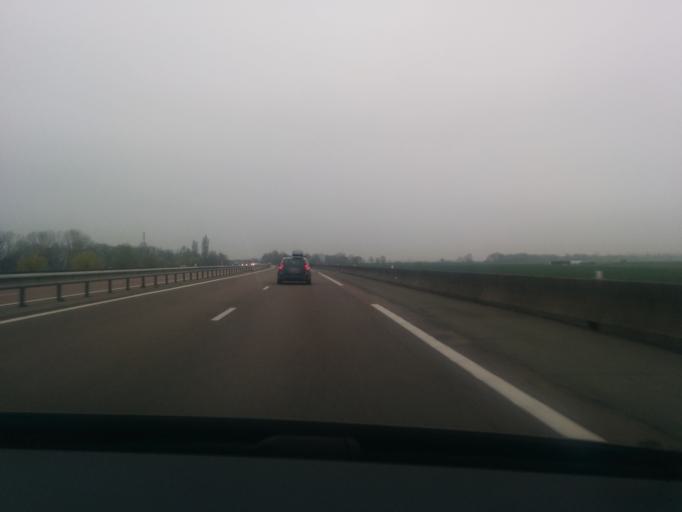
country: FR
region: Bourgogne
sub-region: Departement de la Cote-d'Or
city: Genlis
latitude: 47.2551
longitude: 5.2291
